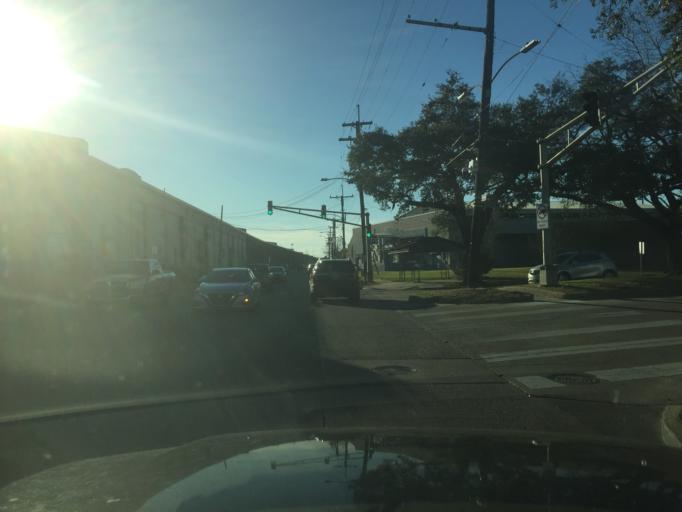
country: US
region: Louisiana
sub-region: Jefferson Parish
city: Harvey
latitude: 29.9184
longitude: -90.0865
